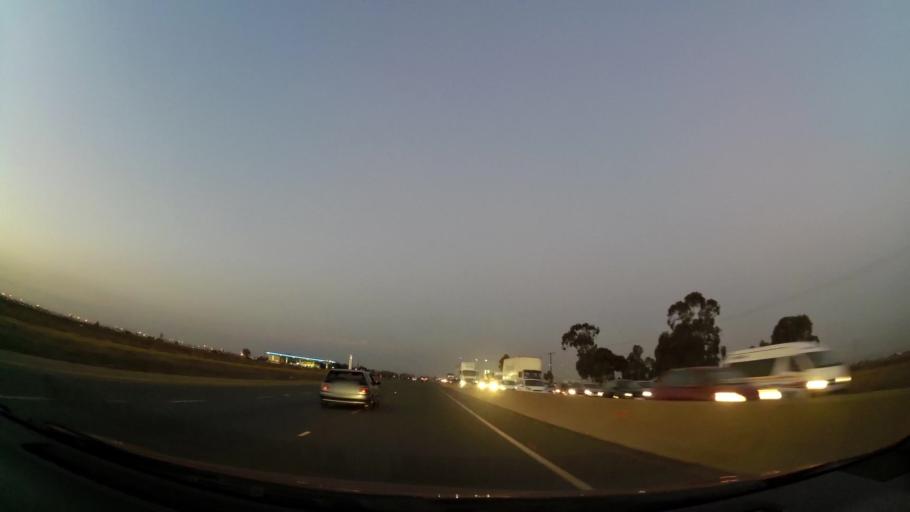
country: ZA
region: Gauteng
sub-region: City of Johannesburg Metropolitan Municipality
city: Soweto
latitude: -26.2977
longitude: 27.8215
